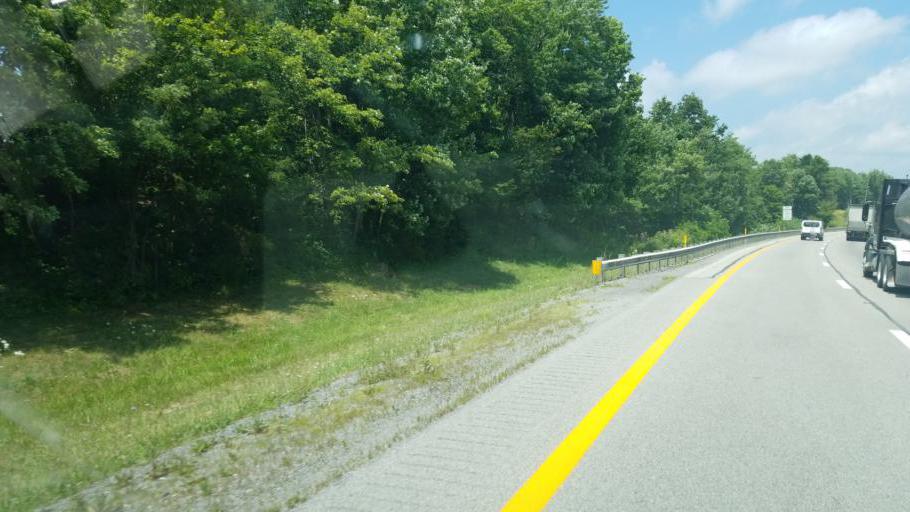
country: US
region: West Virginia
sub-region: Mercer County
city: Princeton
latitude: 37.3984
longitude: -81.0624
